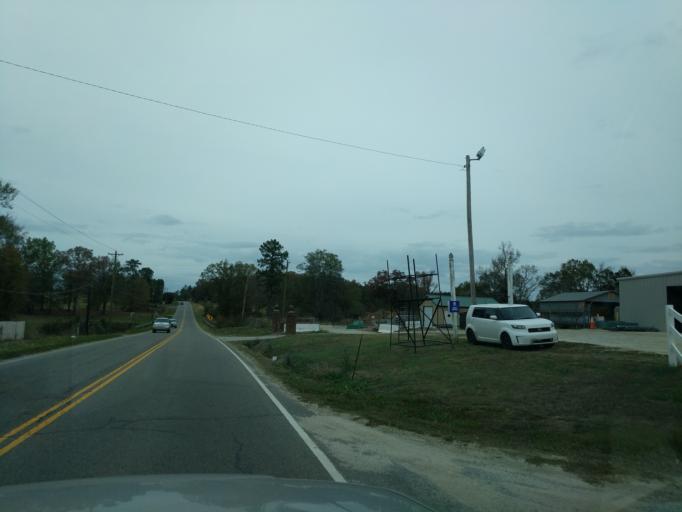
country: US
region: South Carolina
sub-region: Saluda County
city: Saluda
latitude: 34.0156
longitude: -81.7683
